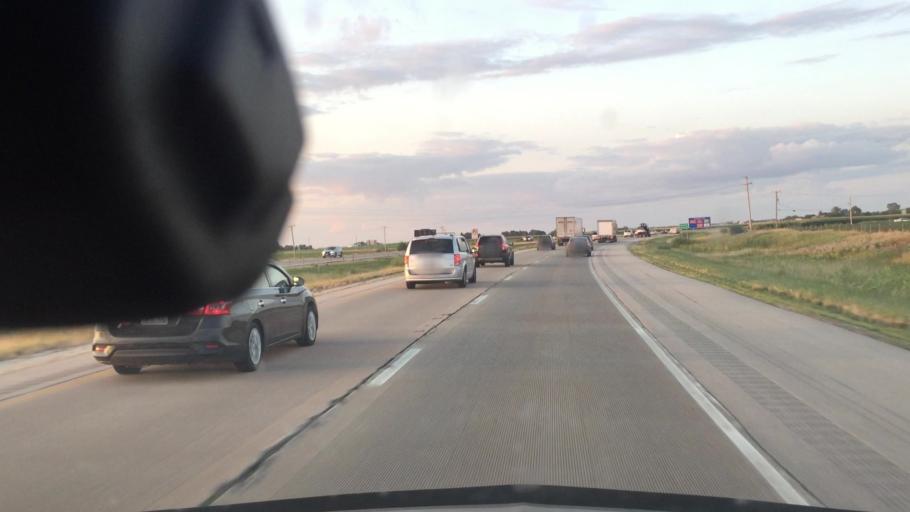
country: US
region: Illinois
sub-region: Livingston County
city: Dwight
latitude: 41.1081
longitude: -88.4465
